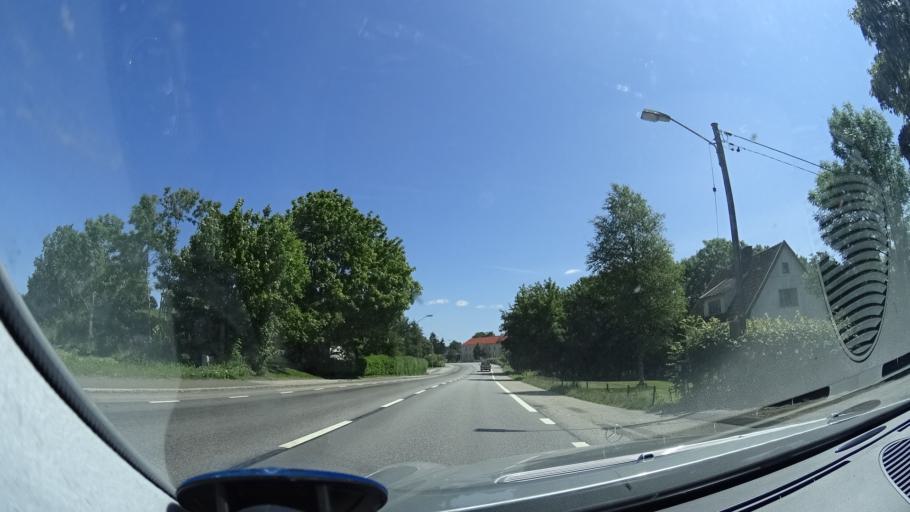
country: SE
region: Skane
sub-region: Horby Kommun
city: Hoerby
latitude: 55.9318
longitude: 13.8204
